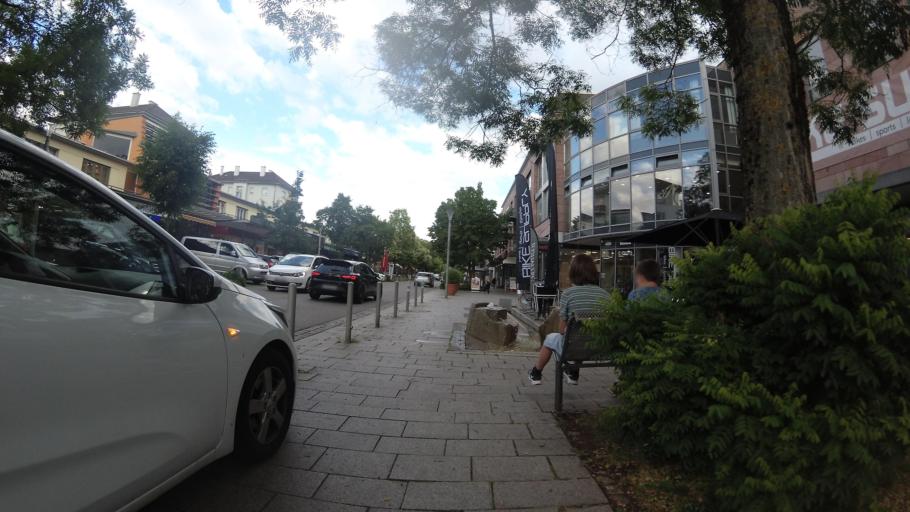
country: DE
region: Baden-Wuerttemberg
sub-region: Freiburg Region
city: Weil am Rhein
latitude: 47.5924
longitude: 7.6130
